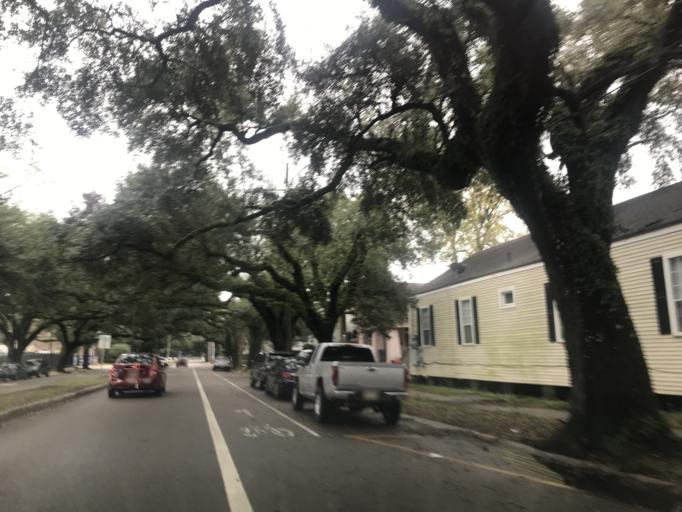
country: US
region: Louisiana
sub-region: Orleans Parish
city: New Orleans
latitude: 29.9736
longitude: -90.1056
